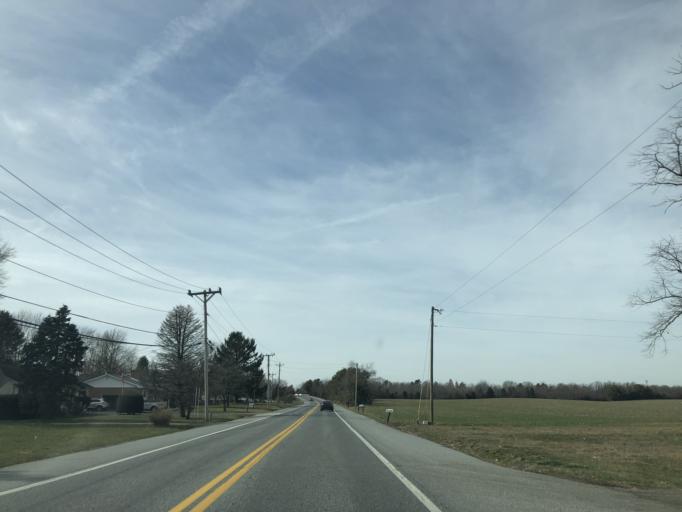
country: US
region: Delaware
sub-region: Kent County
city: Smyrna
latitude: 39.2909
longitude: -75.5877
